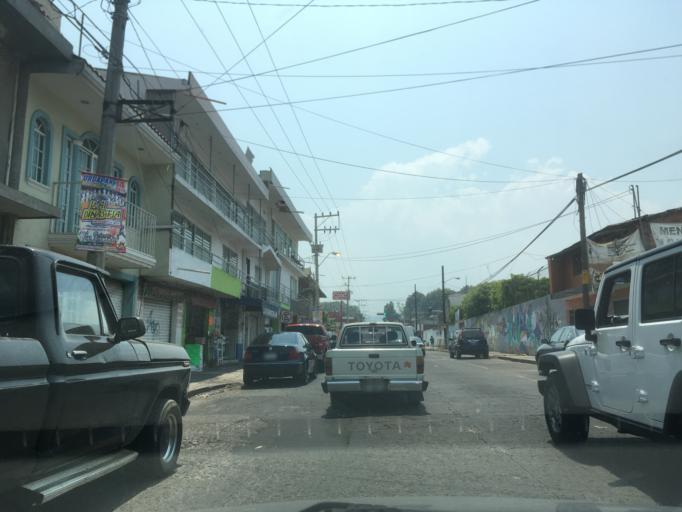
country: MX
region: Michoacan
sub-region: Uruapan
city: Uruapan
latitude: 19.4194
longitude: -102.0456
